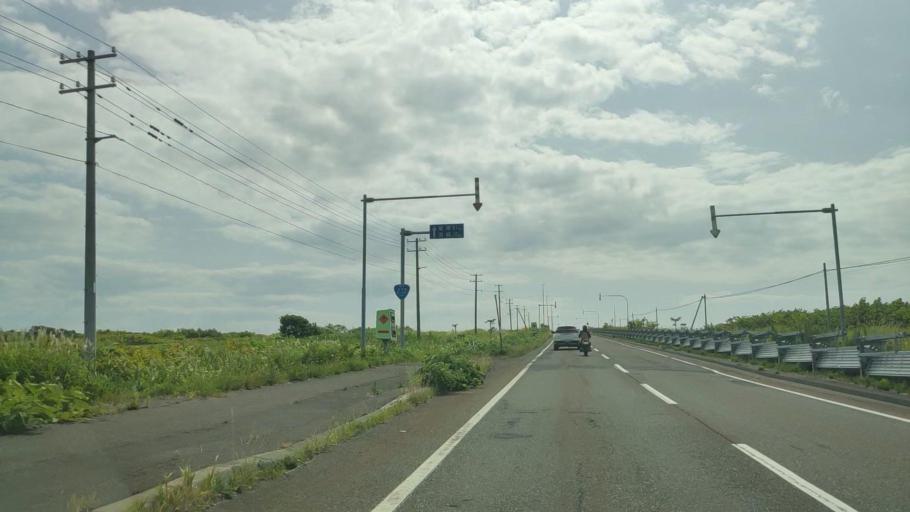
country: JP
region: Hokkaido
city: Rumoi
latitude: 44.4441
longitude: 141.7546
